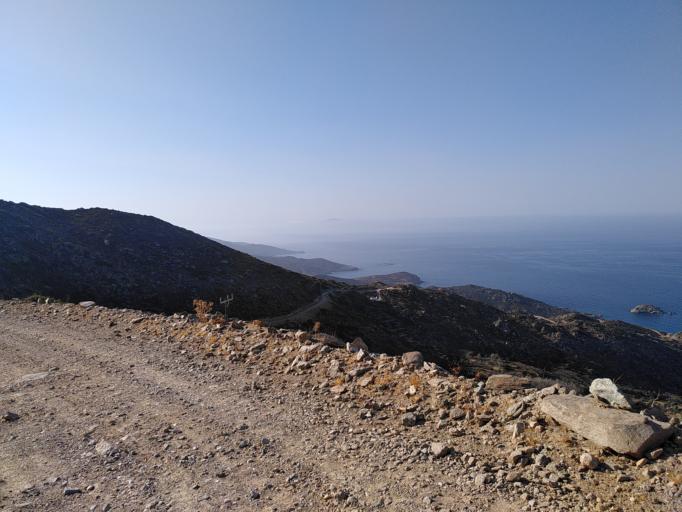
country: GR
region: South Aegean
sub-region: Nomos Kykladon
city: Ios
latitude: 36.7020
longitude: 25.3148
